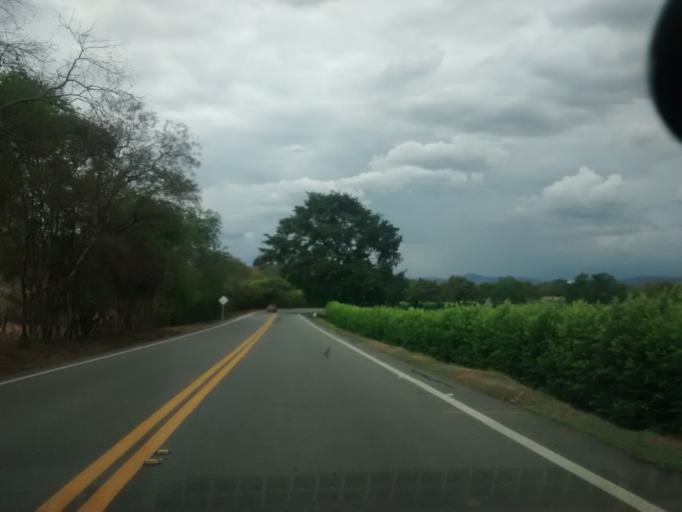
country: CO
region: Cundinamarca
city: Agua de Dios
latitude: 4.4073
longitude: -74.7193
